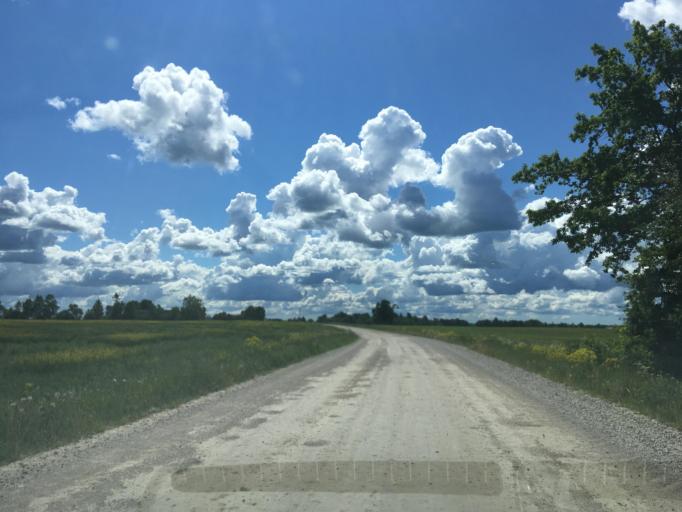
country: EE
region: Harju
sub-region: Nissi vald
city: Turba
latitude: 58.9290
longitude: 24.1529
